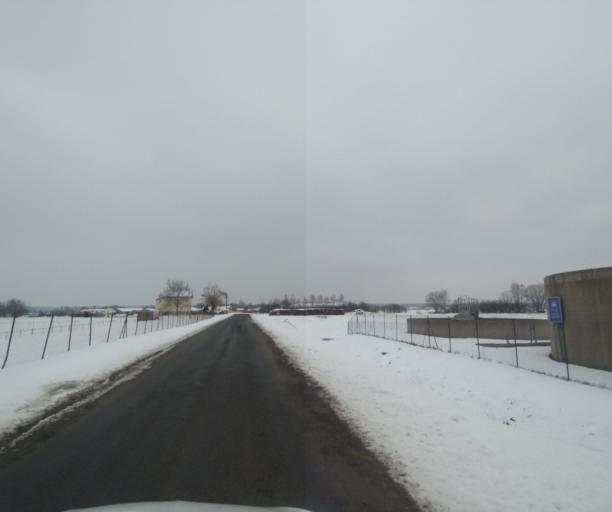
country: FR
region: Champagne-Ardenne
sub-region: Departement de la Haute-Marne
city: Saint-Dizier
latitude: 48.5770
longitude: 4.8922
